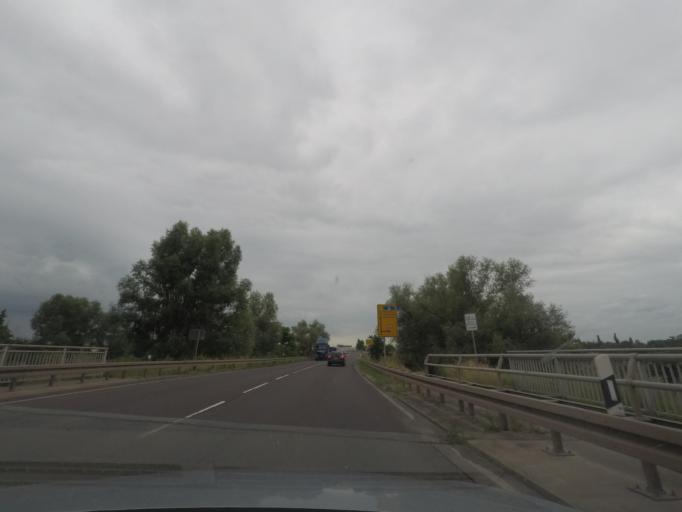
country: DE
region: Saxony-Anhalt
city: Haldensleben I
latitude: 52.2869
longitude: 11.4350
